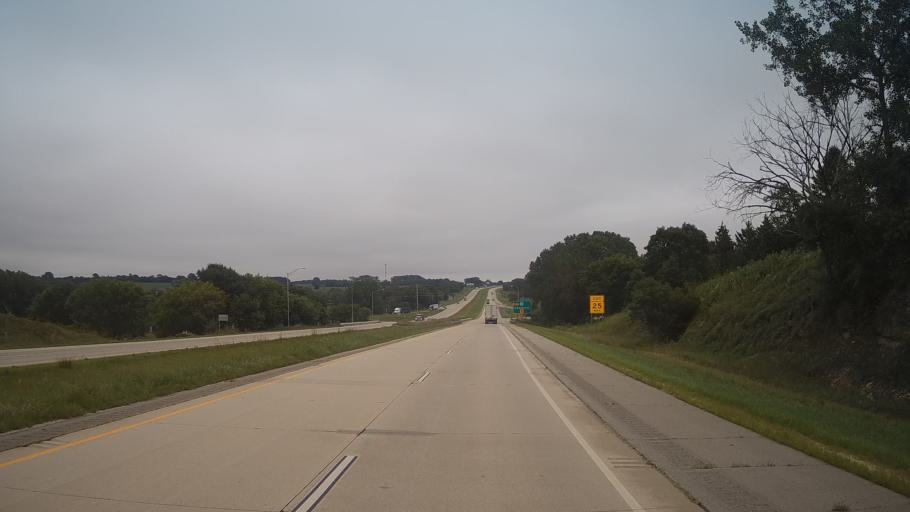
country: US
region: Minnesota
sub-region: Olmsted County
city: Rochester
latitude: 43.9500
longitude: -92.3609
